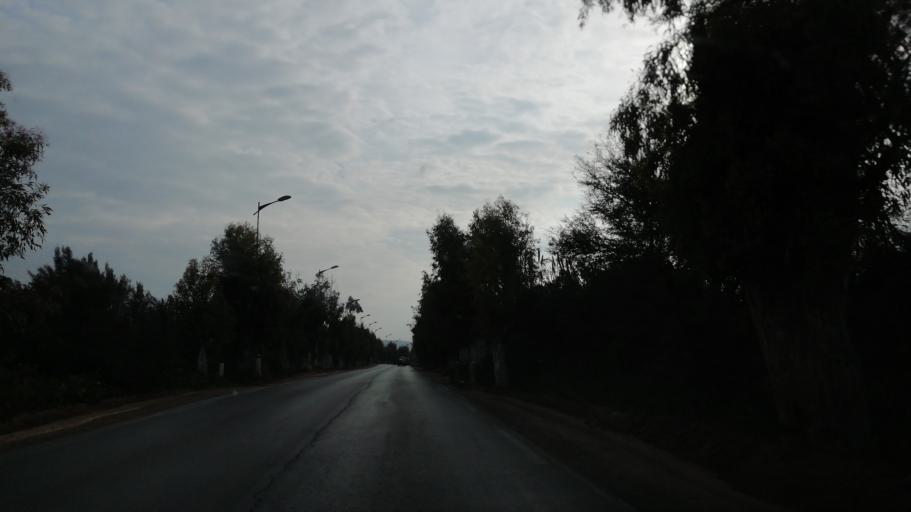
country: DZ
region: Mostaganem
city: Mostaganem
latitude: 35.8760
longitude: 0.0784
